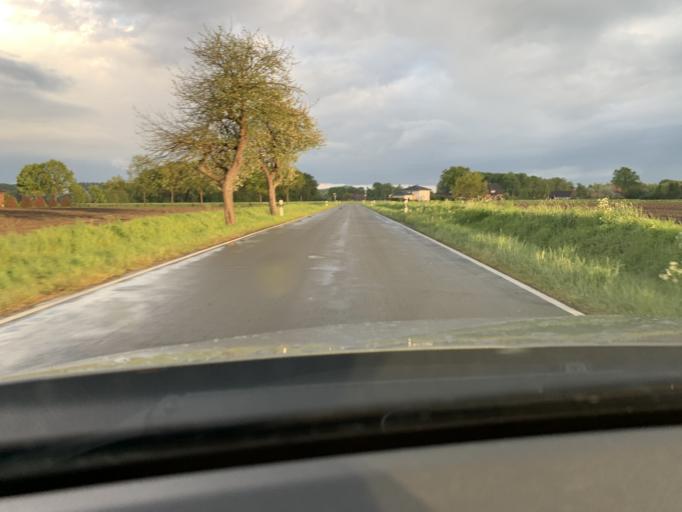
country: DE
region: North Rhine-Westphalia
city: Rietberg
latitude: 51.7810
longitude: 8.3793
